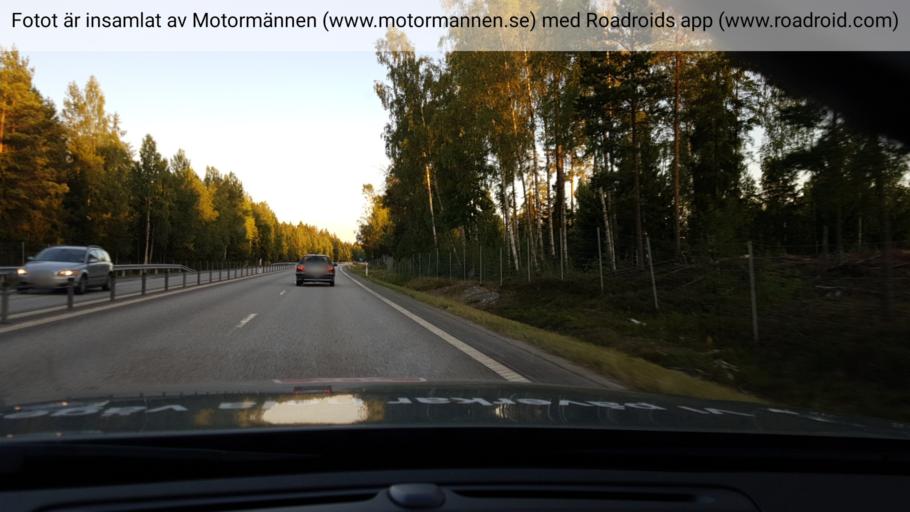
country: SE
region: Vaestmanland
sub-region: Surahammars Kommun
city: Surahammar
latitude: 59.7123
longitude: 16.2449
